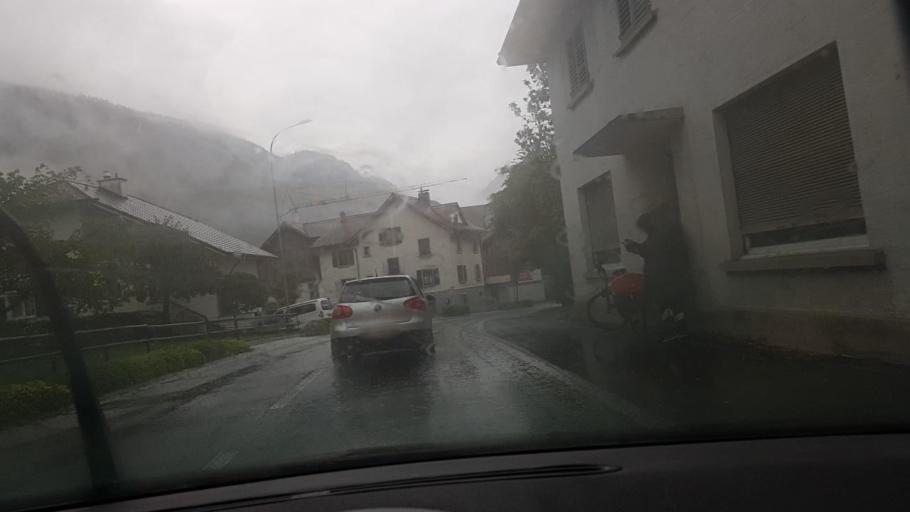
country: LI
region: Balzers
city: Balzers
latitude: 47.0665
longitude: 9.5075
